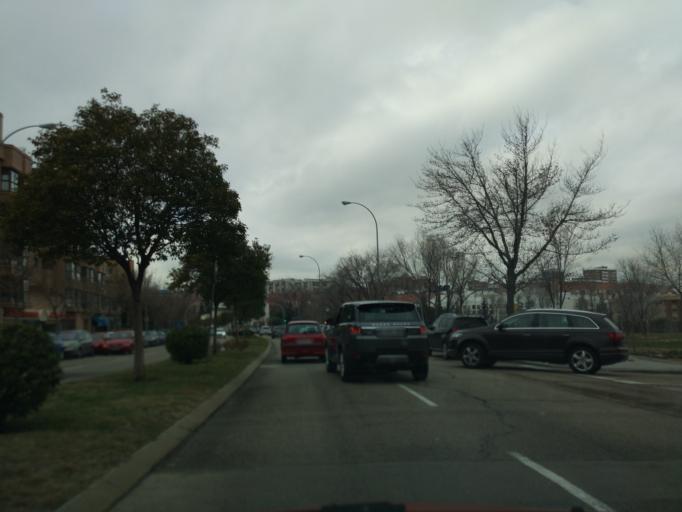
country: ES
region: Madrid
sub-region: Provincia de Madrid
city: Hortaleza
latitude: 40.4592
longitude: -3.6266
